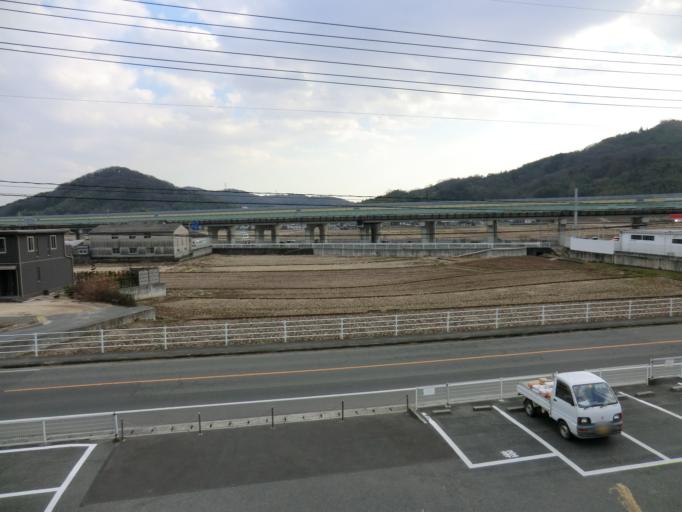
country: JP
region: Okayama
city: Okayama-shi
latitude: 34.7383
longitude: 134.0029
